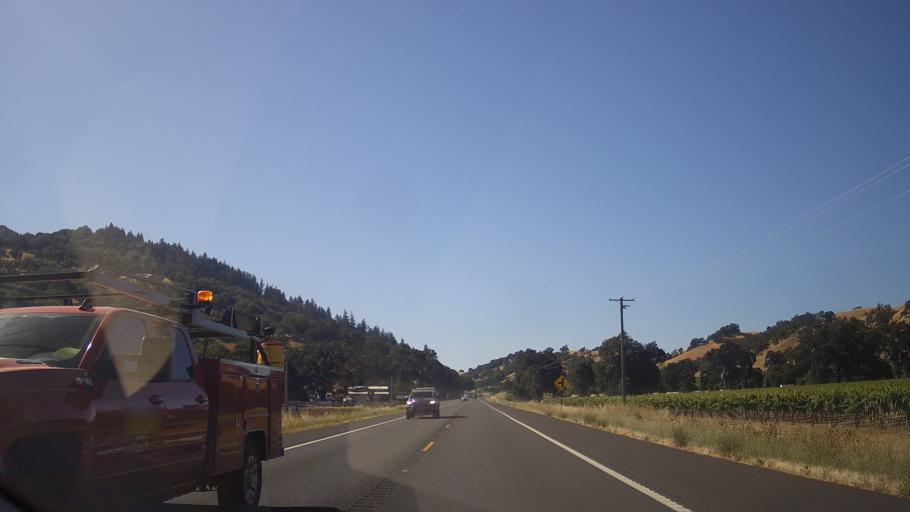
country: US
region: California
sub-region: Mendocino County
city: Talmage
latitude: 39.0519
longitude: -123.1556
